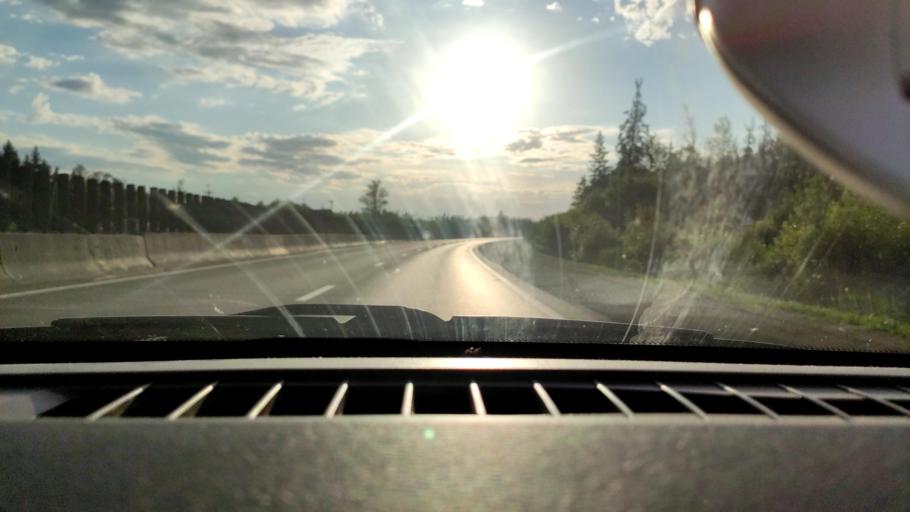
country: RU
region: Perm
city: Kondratovo
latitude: 58.0438
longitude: 56.0098
